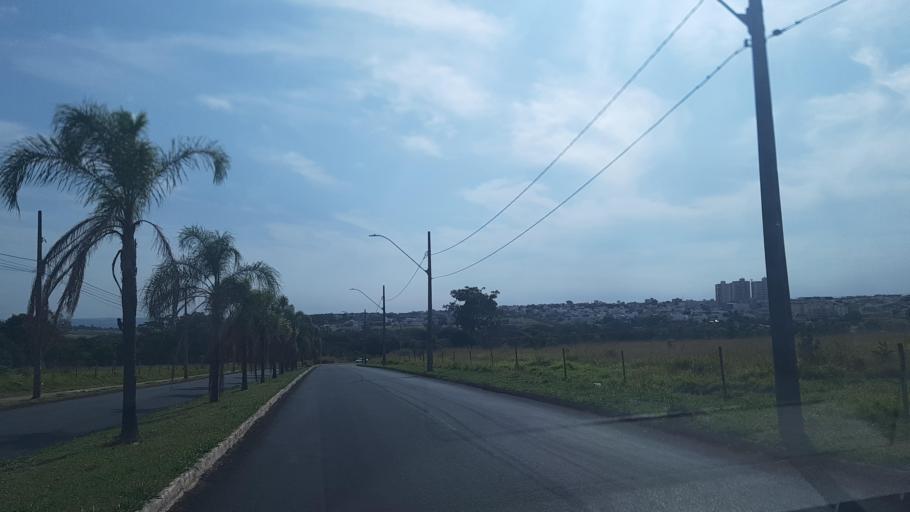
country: BR
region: Minas Gerais
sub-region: Uberlandia
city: Uberlandia
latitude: -18.8809
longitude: -48.2424
